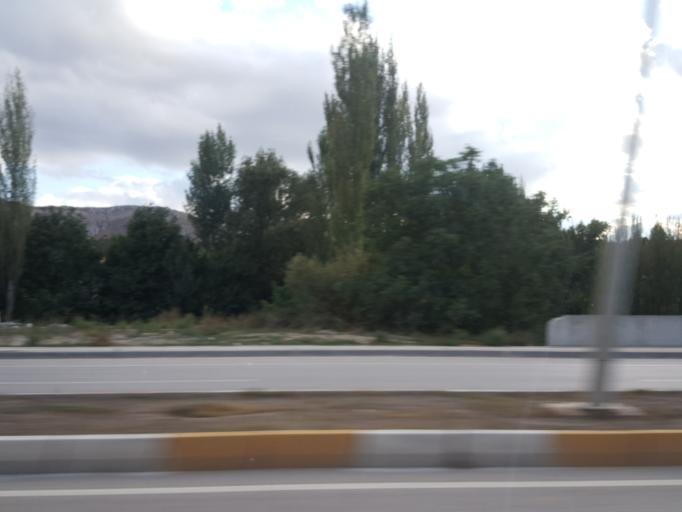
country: TR
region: Tokat
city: Tokat
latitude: 40.3362
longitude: 36.5034
